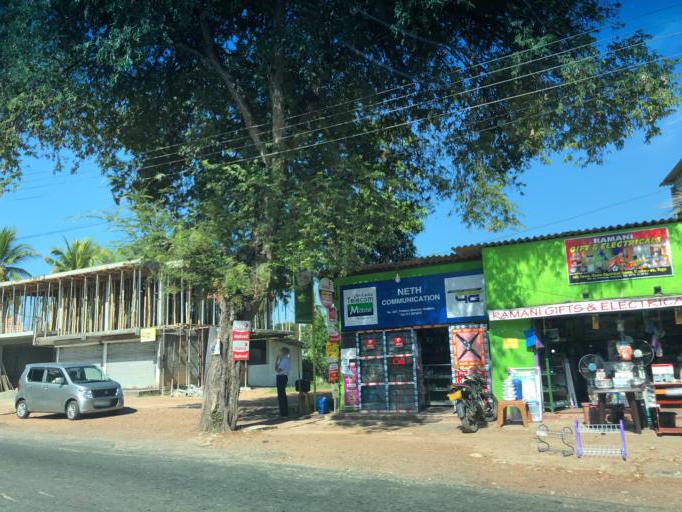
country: LK
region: Western
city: Homagama
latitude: 6.8329
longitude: 79.9647
